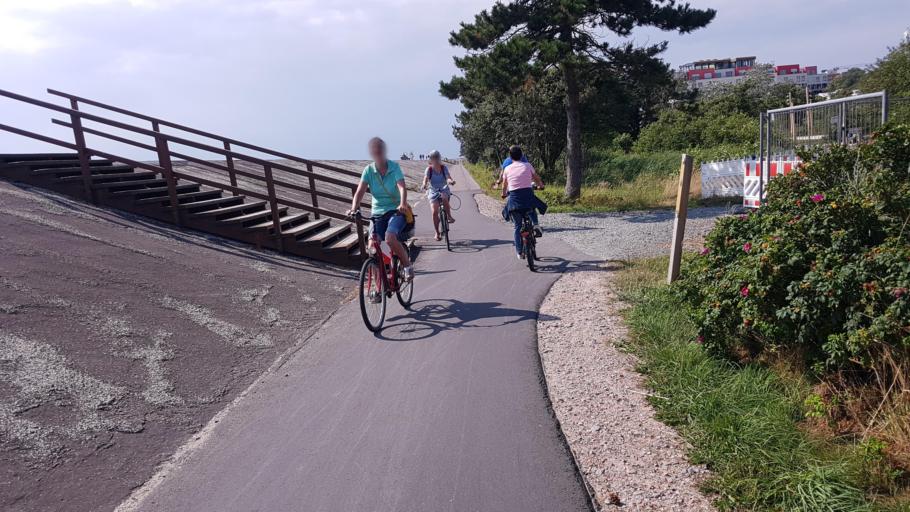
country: DE
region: Schleswig-Holstein
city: Sankt Peter-Ording
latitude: 54.3068
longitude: 8.6162
